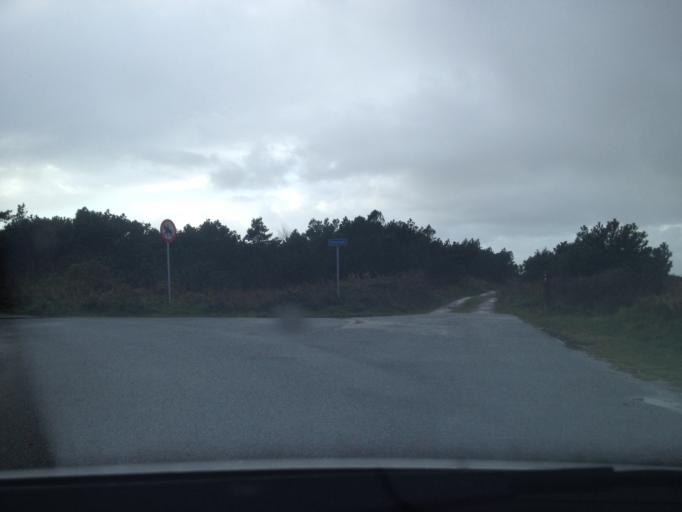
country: DE
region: Schleswig-Holstein
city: List
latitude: 55.1589
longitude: 8.5197
